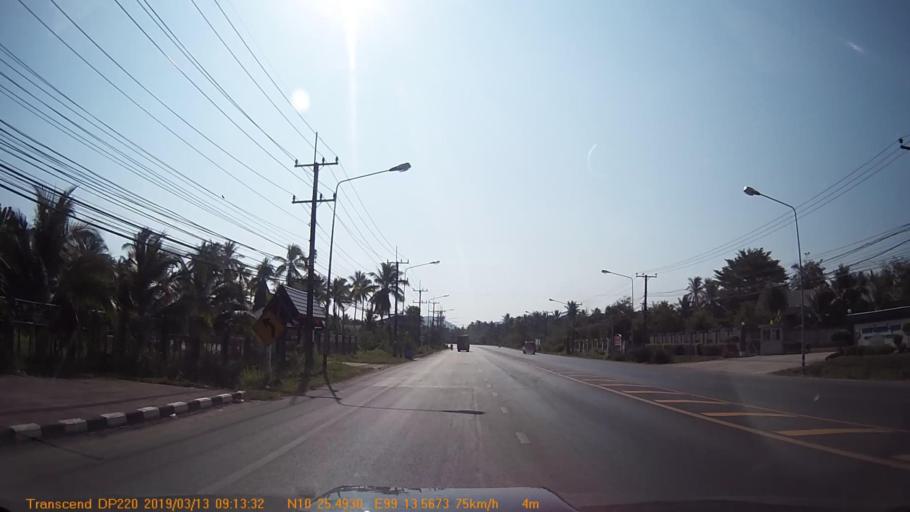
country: TH
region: Chumphon
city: Chumphon
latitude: 10.4247
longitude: 99.2264
